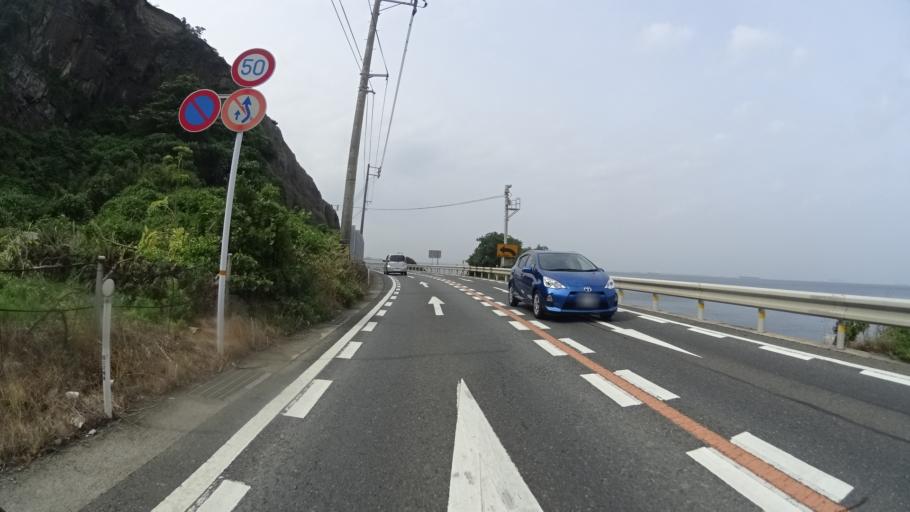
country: JP
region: Yamaguchi
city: Shimonoseki
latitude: 34.0570
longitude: 130.9122
